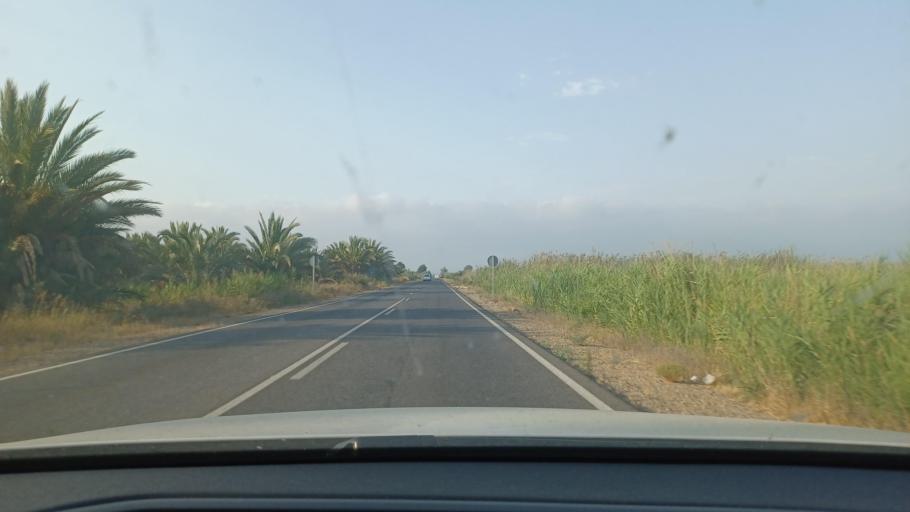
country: ES
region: Valencia
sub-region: Provincia de Alicante
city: Dolores
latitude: 38.1754
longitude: -0.7020
